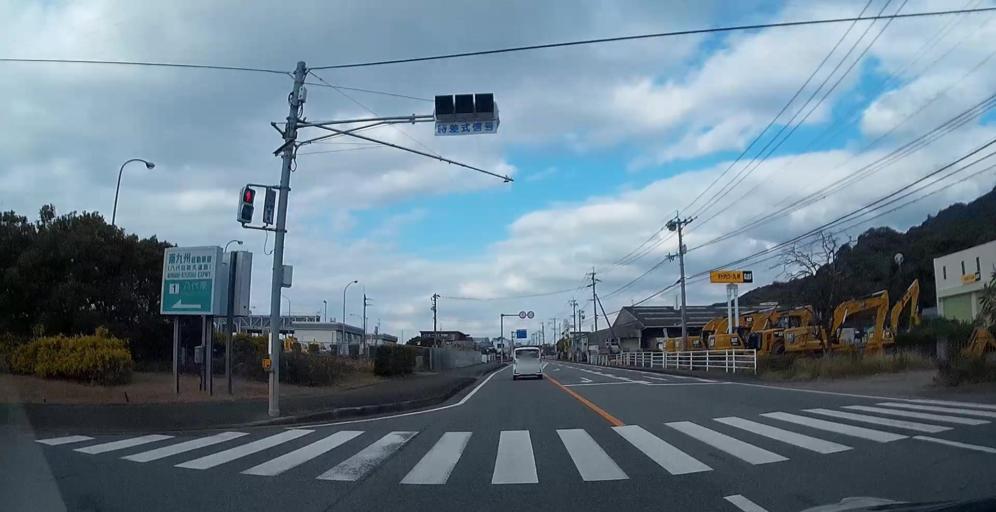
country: JP
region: Kumamoto
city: Yatsushiro
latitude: 32.4613
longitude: 130.6017
